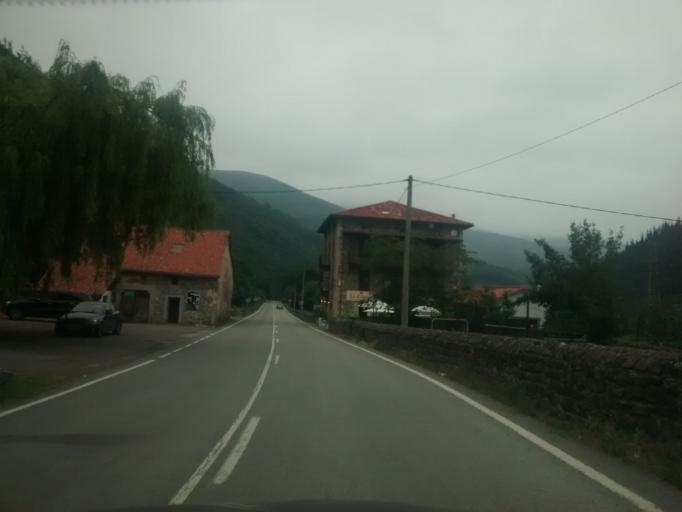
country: ES
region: Cantabria
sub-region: Provincia de Cantabria
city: Ruente
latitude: 43.1801
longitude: -4.2985
